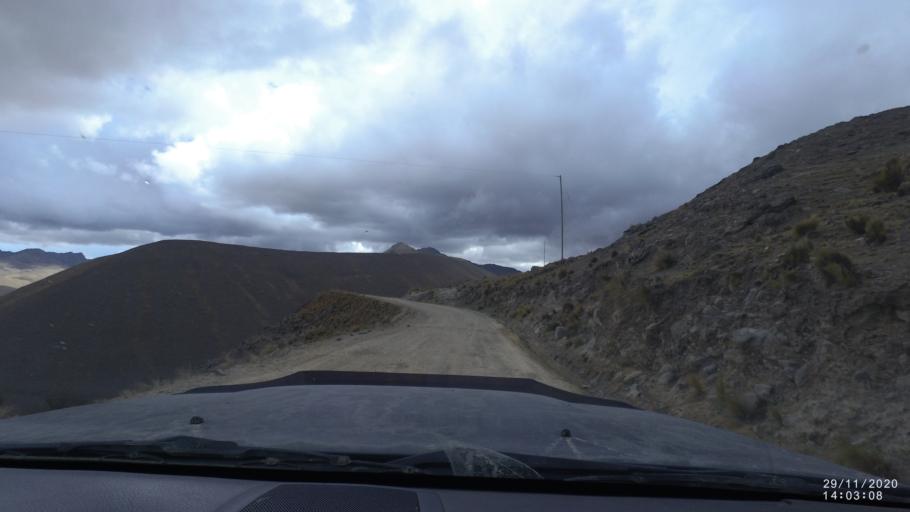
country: BO
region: Cochabamba
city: Sipe Sipe
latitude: -17.1941
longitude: -66.3756
